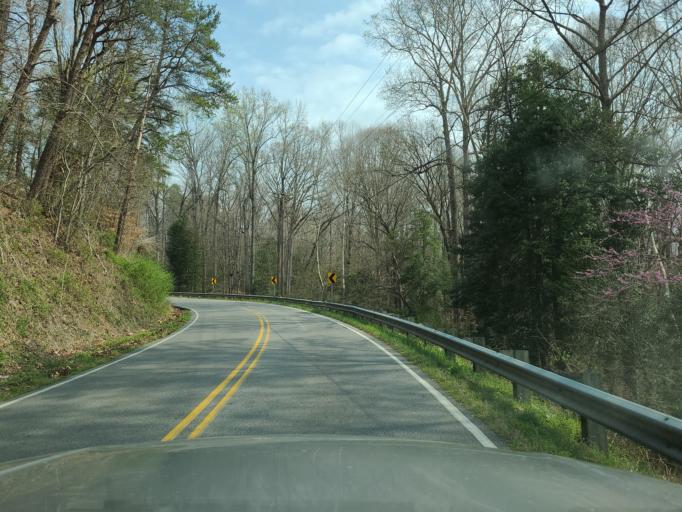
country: US
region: North Carolina
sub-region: Gaston County
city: Ranlo
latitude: 35.3101
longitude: -81.1060
